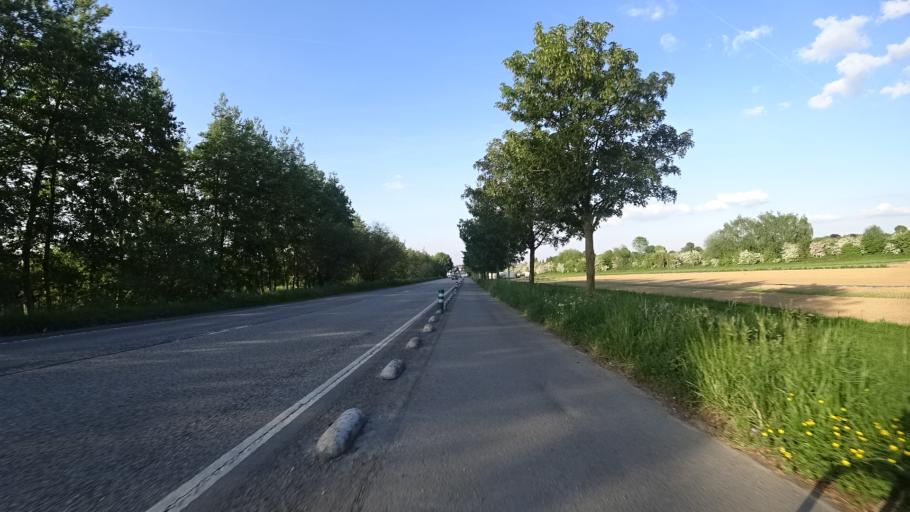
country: BE
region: Wallonia
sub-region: Province de Namur
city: Eghezee
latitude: 50.5816
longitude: 4.9062
